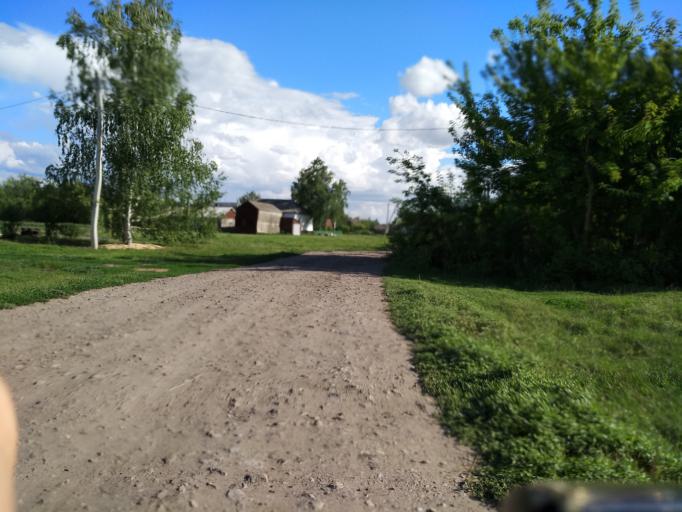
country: RU
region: Lipetsk
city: Dobrinka
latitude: 52.0305
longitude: 40.5626
